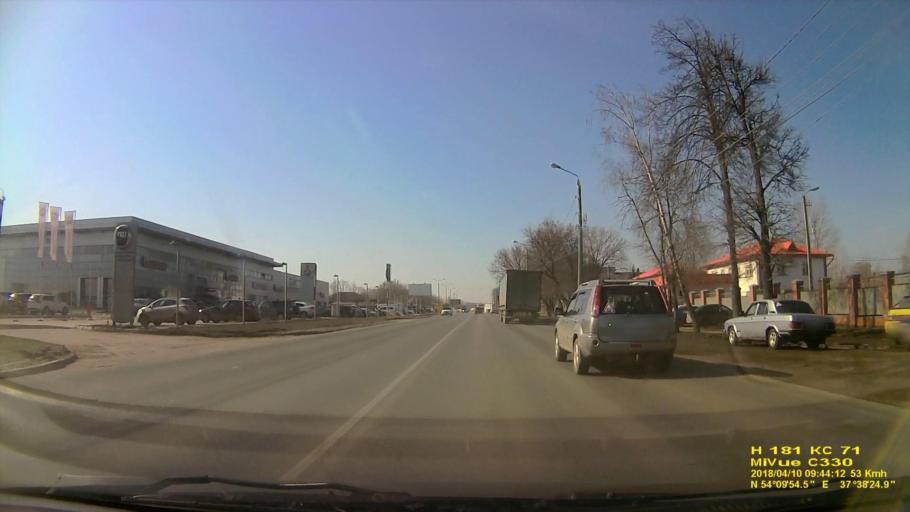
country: RU
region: Tula
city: Tula
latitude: 54.1648
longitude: 37.6426
